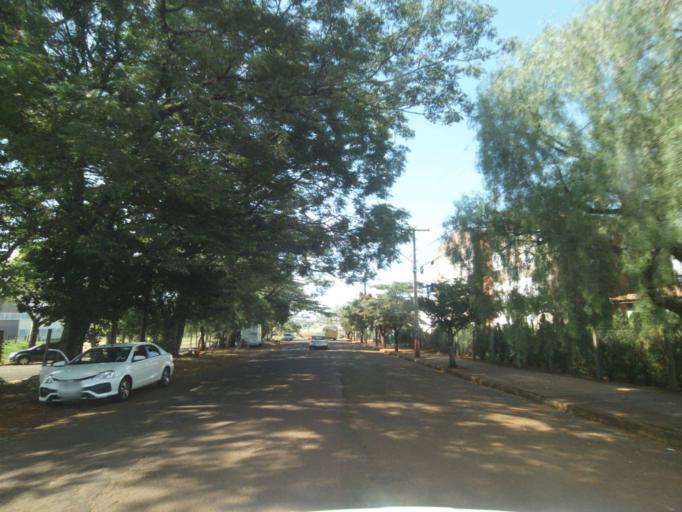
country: BR
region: Parana
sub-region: Londrina
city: Londrina
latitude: -23.3262
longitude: -51.1940
